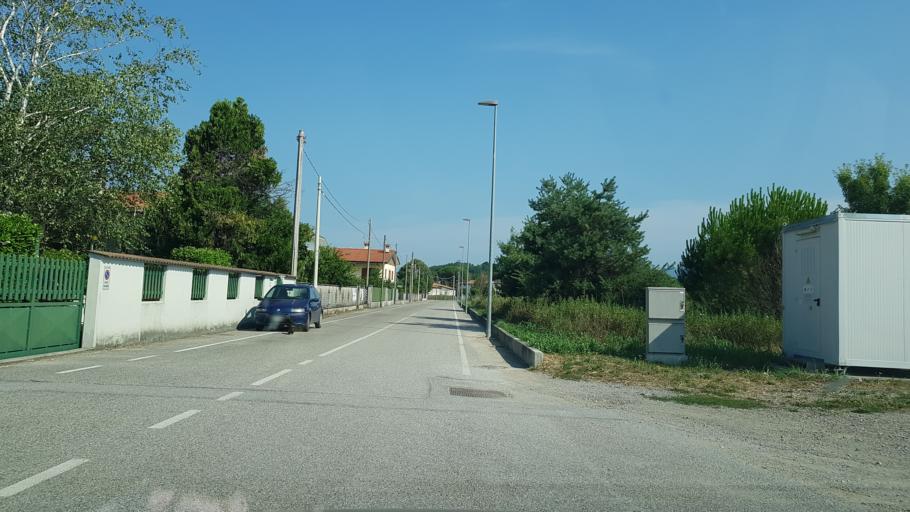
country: IT
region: Friuli Venezia Giulia
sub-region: Provincia di Gorizia
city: Mossa
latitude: 45.9362
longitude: 13.5516
